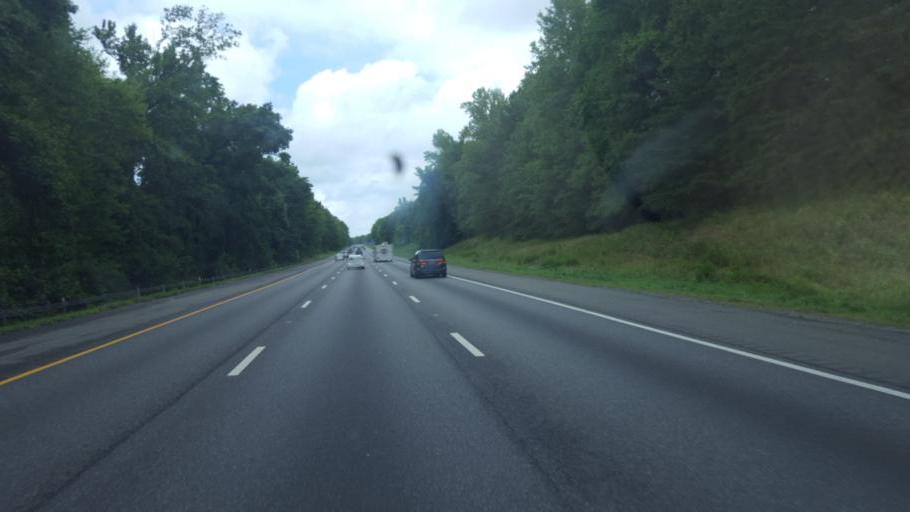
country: US
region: Virginia
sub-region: Hanover County
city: Ashland
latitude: 37.9017
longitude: -77.4587
